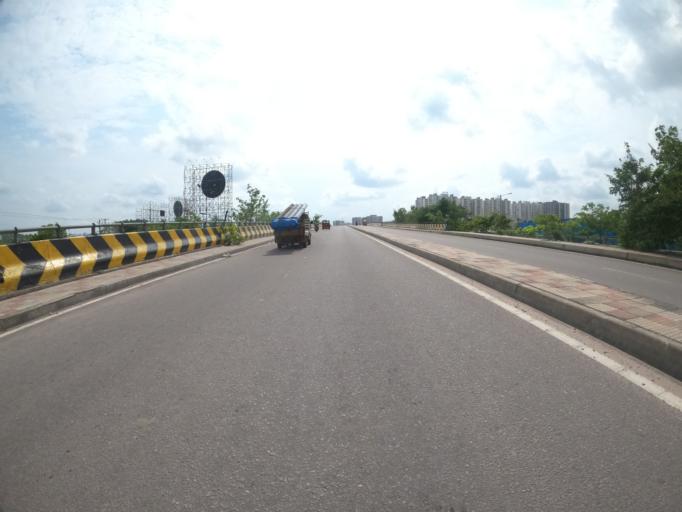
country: IN
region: Telangana
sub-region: Hyderabad
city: Hyderabad
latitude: 17.3858
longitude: 78.3530
